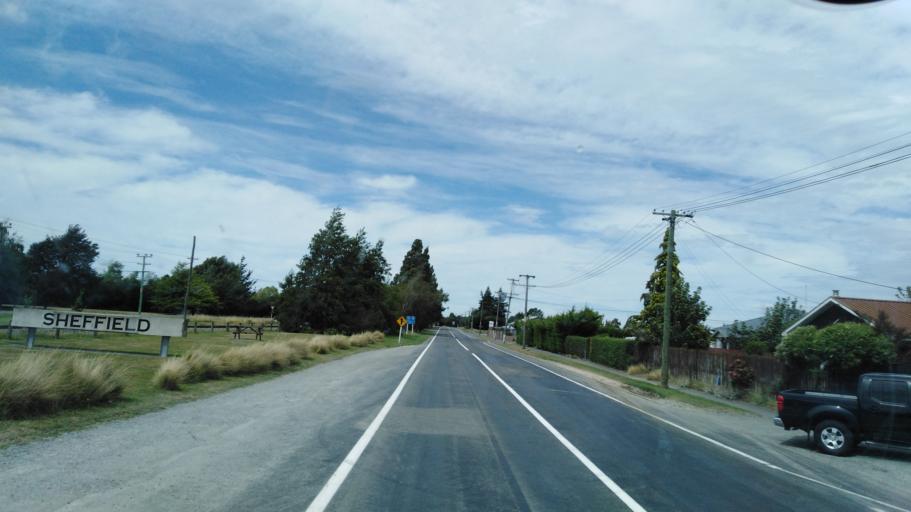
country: NZ
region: Canterbury
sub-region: Selwyn District
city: Darfield
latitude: -43.3893
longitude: 172.0203
